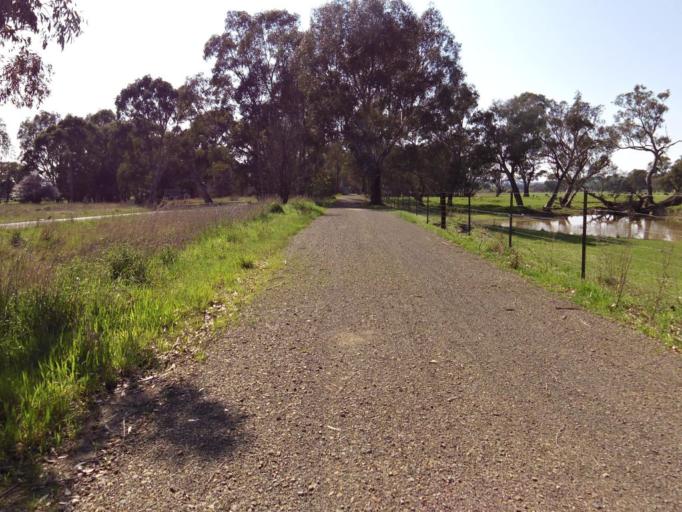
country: AU
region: Victoria
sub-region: Murrindindi
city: Alexandra
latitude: -37.1521
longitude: 145.5790
